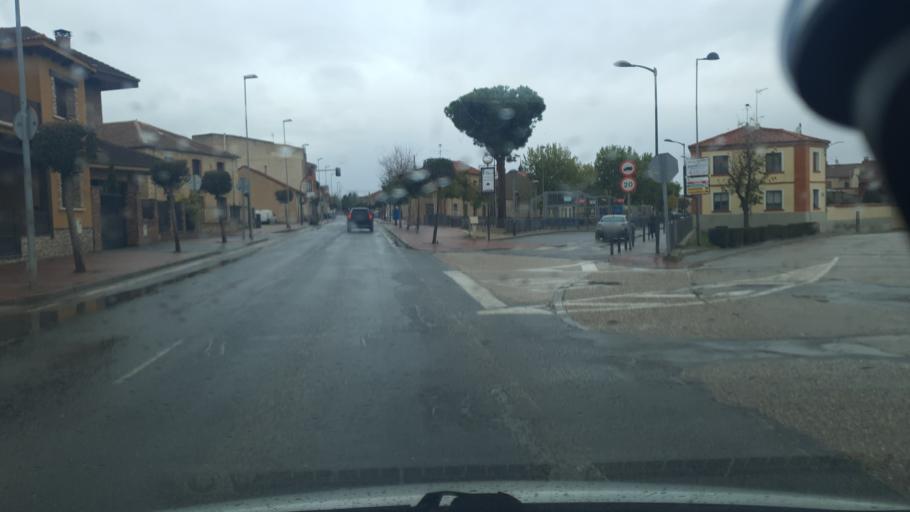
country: ES
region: Castille and Leon
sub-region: Provincia de Segovia
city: Carbonero el Mayor
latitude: 41.1184
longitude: -4.2642
